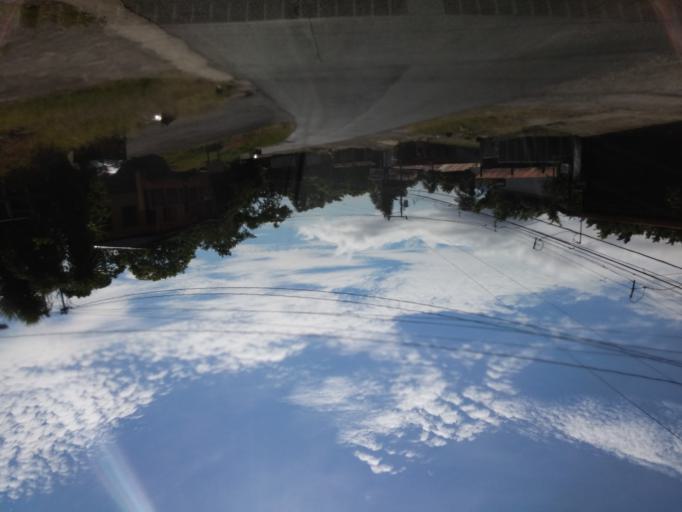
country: CR
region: Heredia
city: Llorente
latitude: 10.0259
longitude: -84.1743
